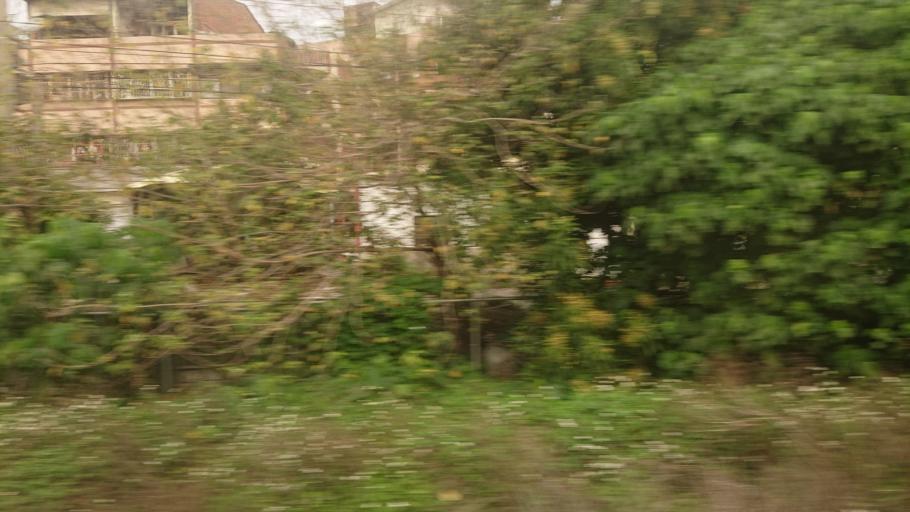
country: TW
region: Taiwan
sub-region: Changhua
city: Chang-hua
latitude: 24.0907
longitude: 120.5522
